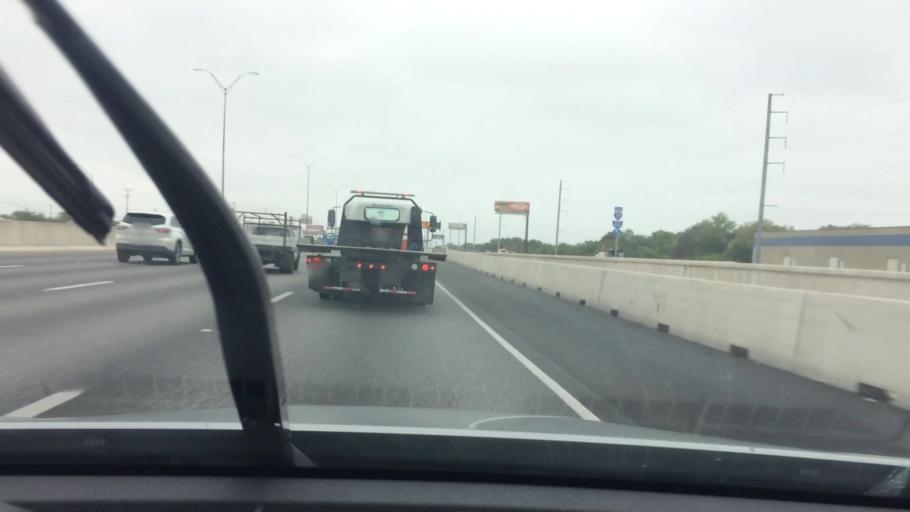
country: US
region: Texas
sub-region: Bexar County
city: Windcrest
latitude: 29.5009
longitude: -98.4005
